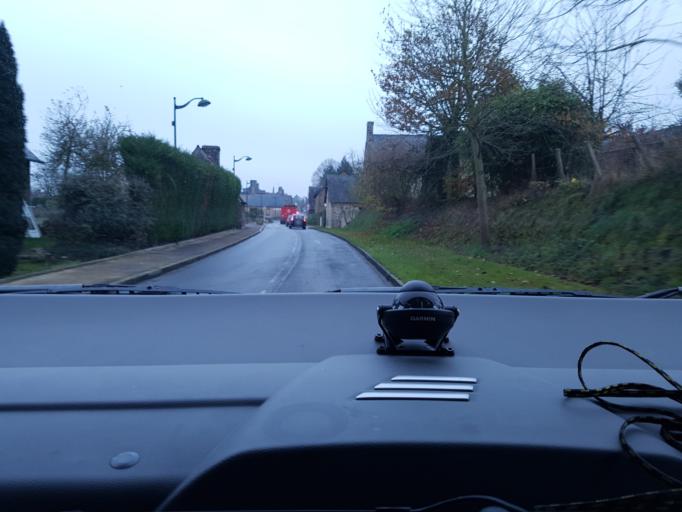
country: FR
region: Brittany
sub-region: Departement d'Ille-et-Vilaine
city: Antrain
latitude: 48.4634
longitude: -1.4461
